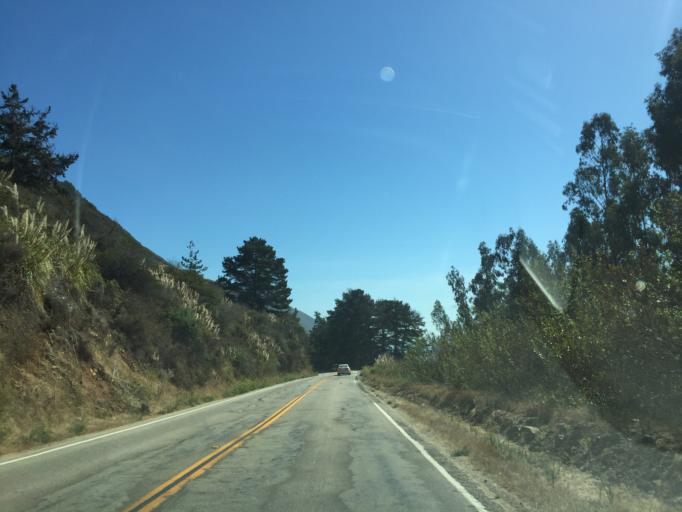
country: US
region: California
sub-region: Monterey County
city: Greenfield
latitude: 35.9935
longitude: -121.4969
